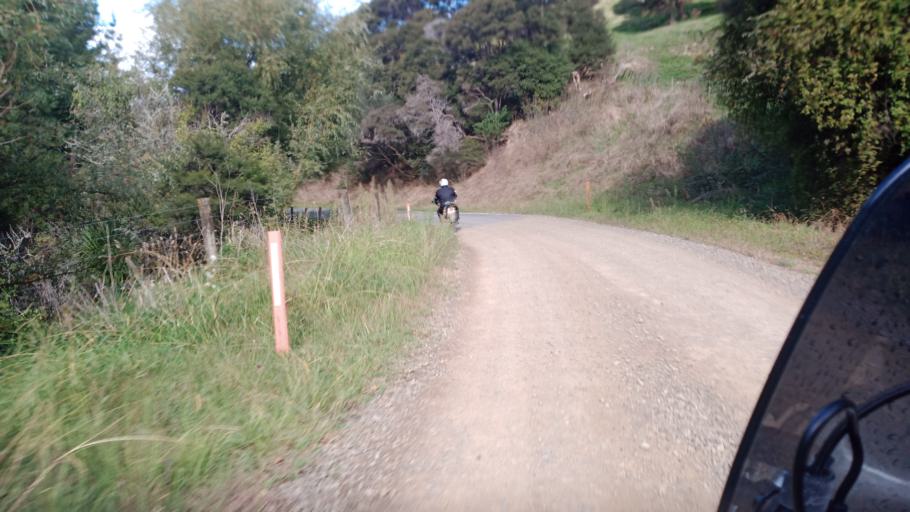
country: NZ
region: Gisborne
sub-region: Gisborne District
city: Gisborne
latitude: -38.4609
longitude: 177.6443
